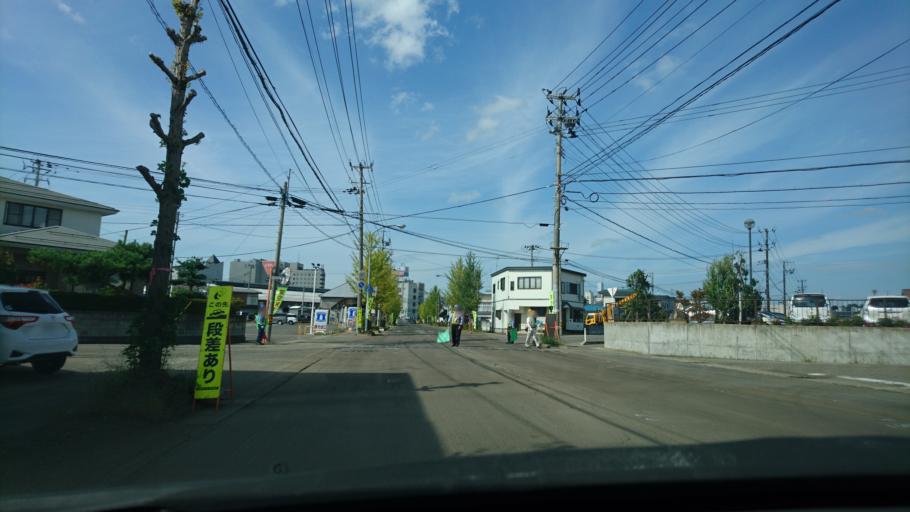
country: JP
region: Akita
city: Yokotemachi
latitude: 39.3068
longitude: 140.5635
